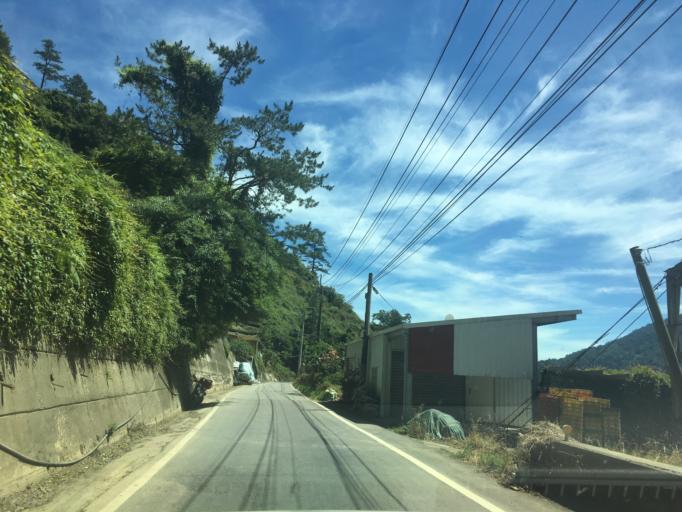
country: TW
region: Taiwan
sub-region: Nantou
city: Puli
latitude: 24.2318
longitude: 121.2533
